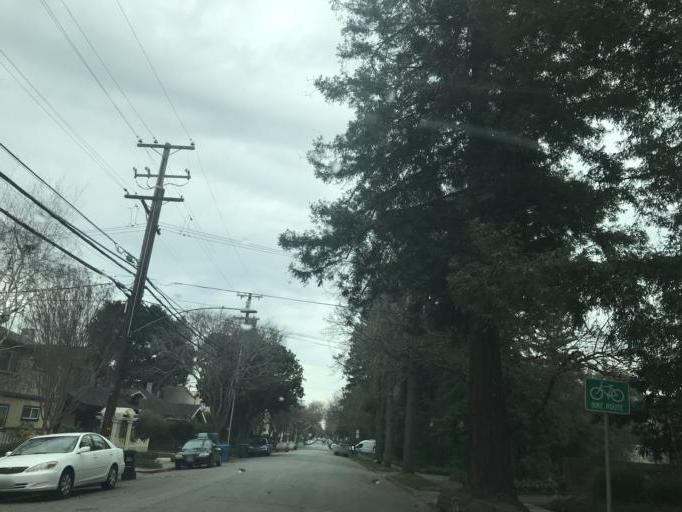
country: US
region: California
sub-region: San Mateo County
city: Menlo Park
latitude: 37.4491
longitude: -122.1666
